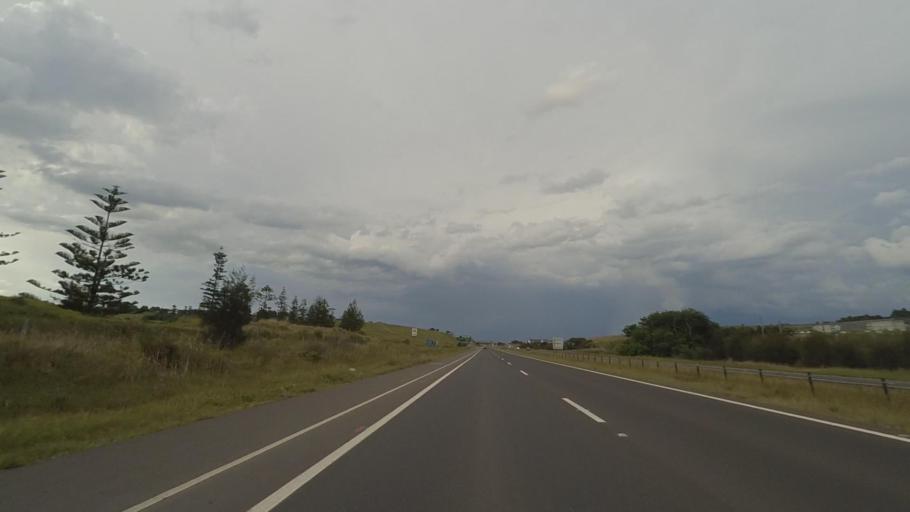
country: AU
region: New South Wales
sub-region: Shellharbour
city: Croom
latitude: -34.5967
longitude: 150.8421
